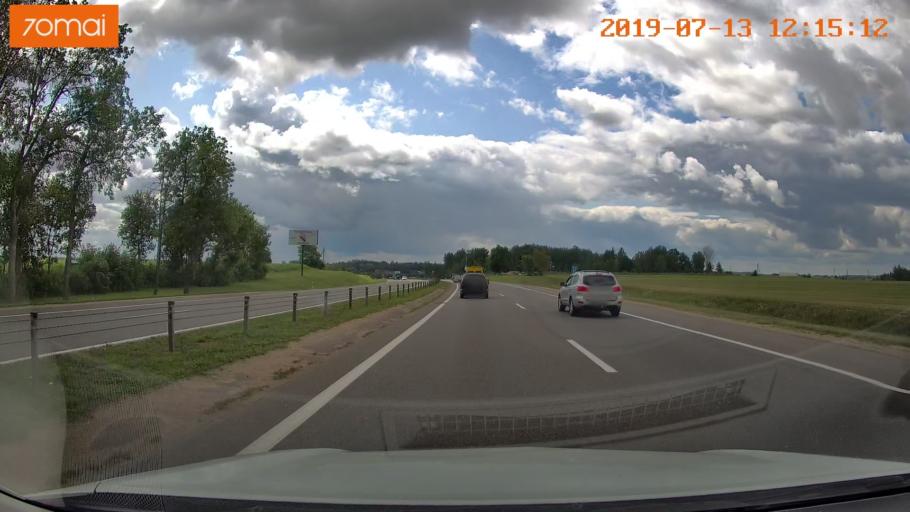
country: BY
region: Minsk
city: Samakhvalavichy
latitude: 53.7525
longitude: 27.5145
